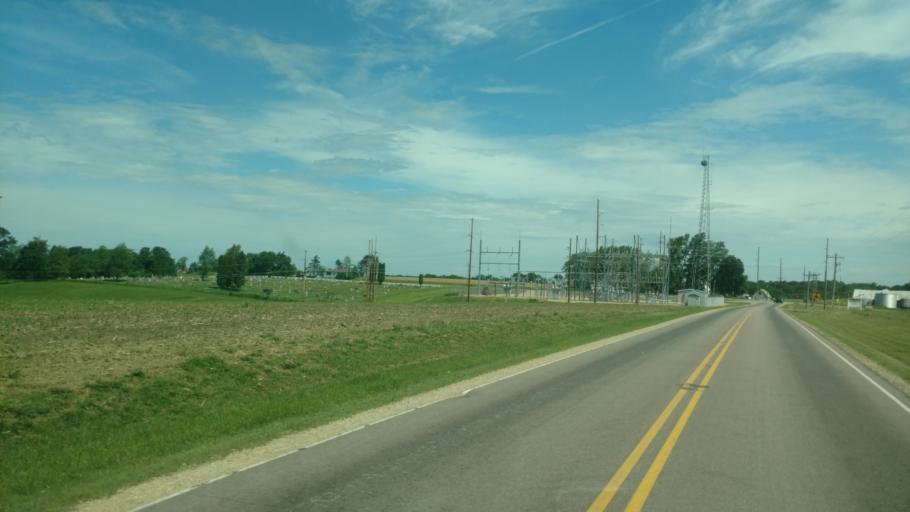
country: US
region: Wisconsin
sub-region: Vernon County
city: Hillsboro
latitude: 43.6653
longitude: -90.4588
